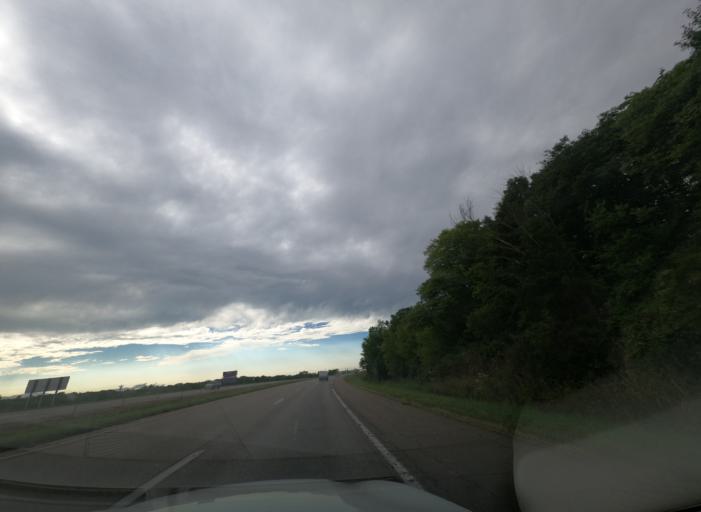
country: US
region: Missouri
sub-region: Sainte Genevieve County
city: Sainte Genevieve
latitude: 37.9290
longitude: -90.1118
